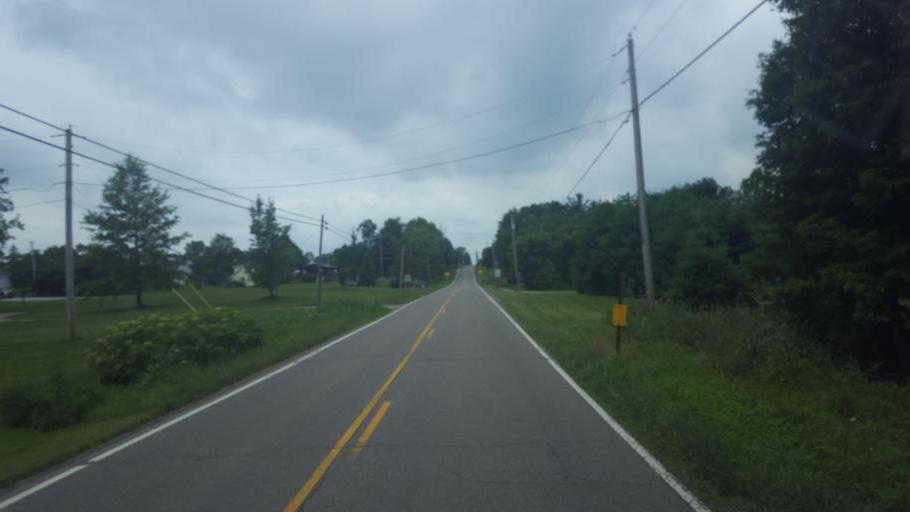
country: US
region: Ohio
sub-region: Licking County
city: Granville
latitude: 40.1523
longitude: -82.5160
